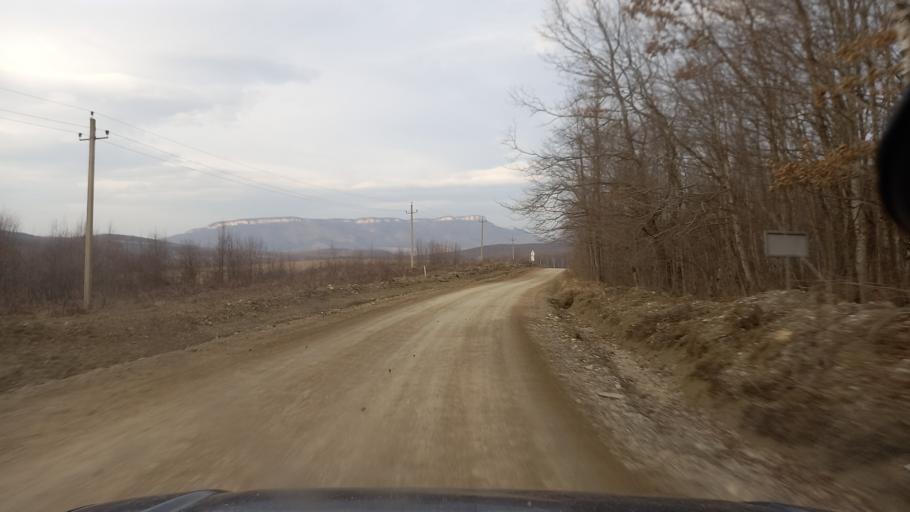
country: RU
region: Adygeya
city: Kamennomostskiy
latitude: 44.1556
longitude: 40.2419
